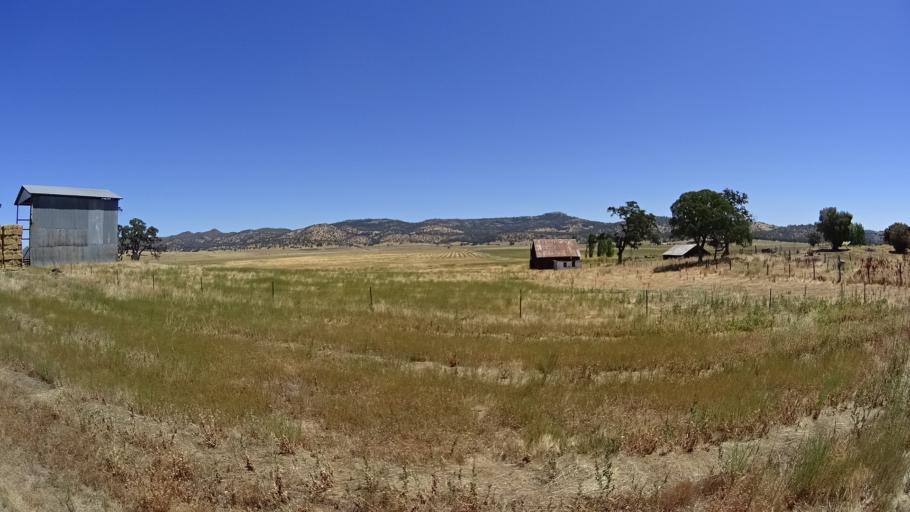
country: US
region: California
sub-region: Calaveras County
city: Copperopolis
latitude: 38.0289
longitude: -120.7168
